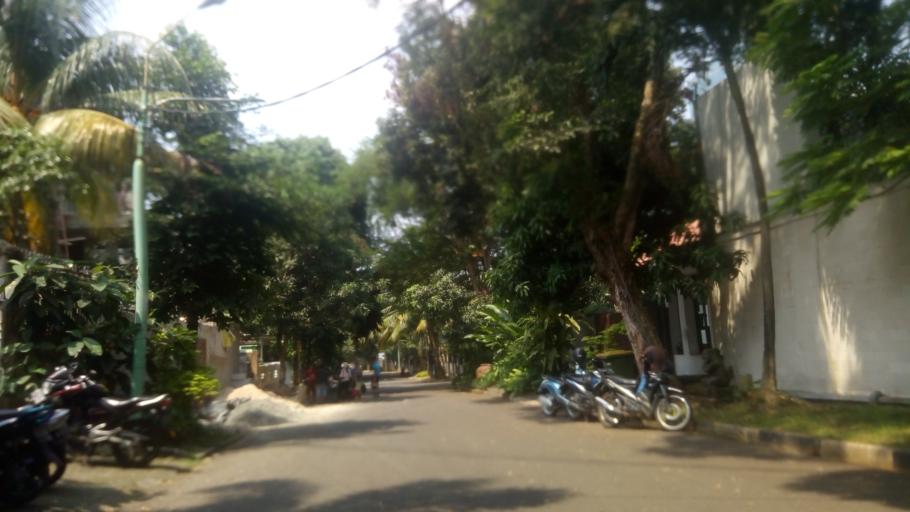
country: ID
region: Jakarta Raya
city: Jakarta
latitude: -6.2378
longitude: 106.8329
